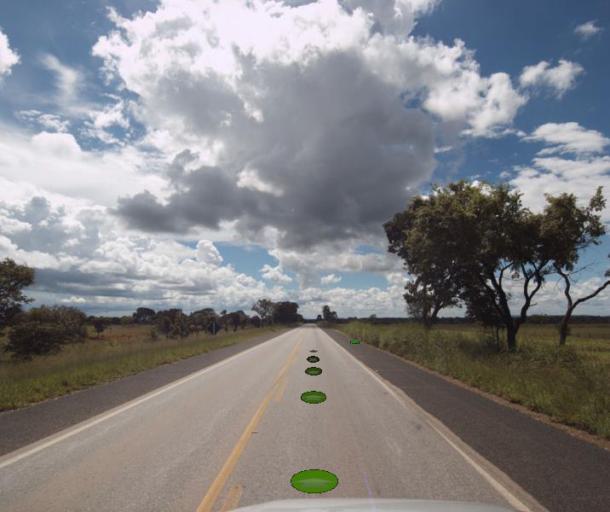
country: BR
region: Goias
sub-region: Uruacu
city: Uruacu
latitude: -14.0086
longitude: -49.0857
